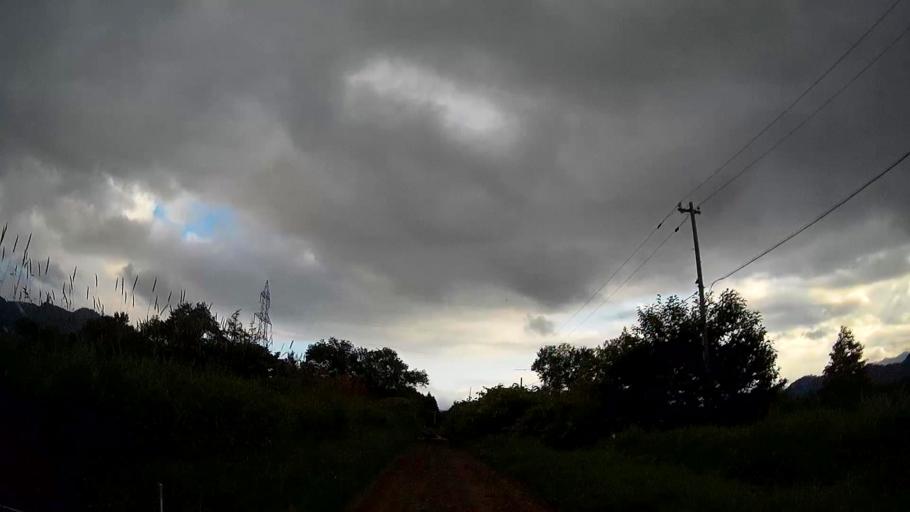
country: JP
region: Hokkaido
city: Nanae
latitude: 42.1220
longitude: 140.4068
